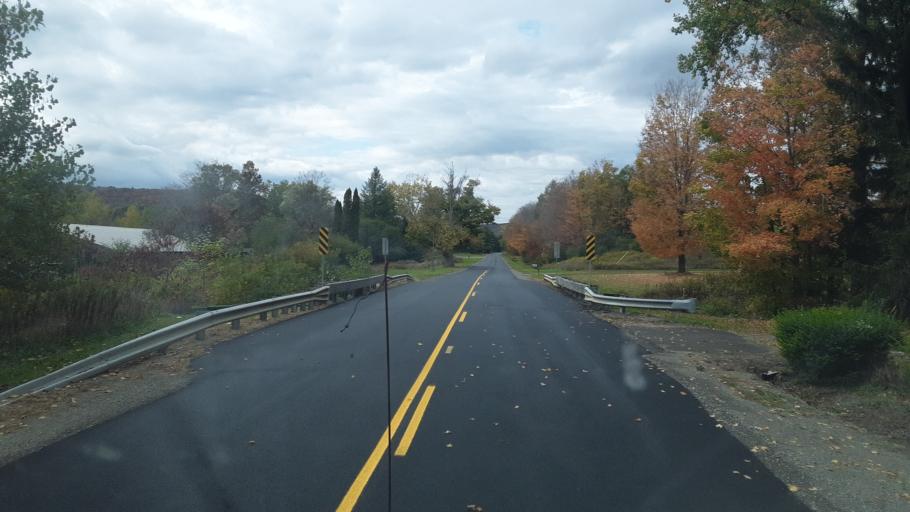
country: US
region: New York
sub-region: Allegany County
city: Alfred
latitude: 42.3663
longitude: -77.7745
